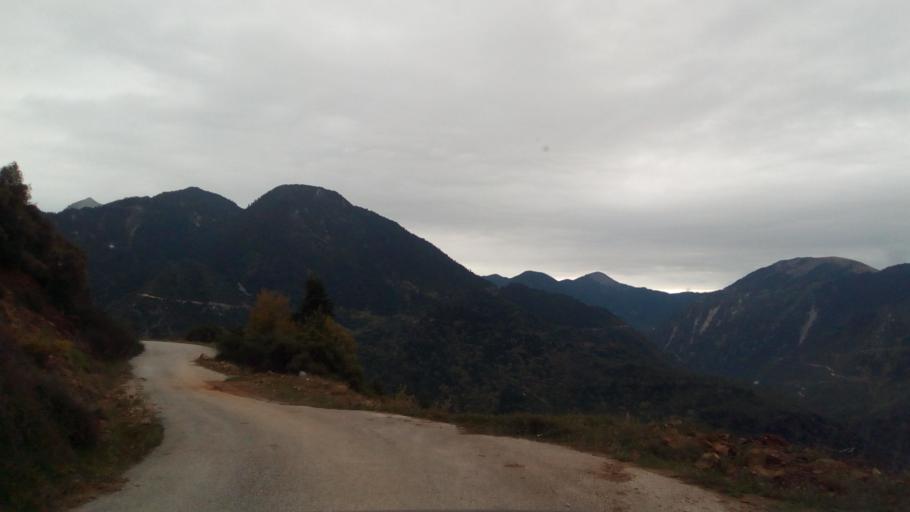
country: GR
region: West Greece
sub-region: Nomos Aitolias kai Akarnanias
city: Thermo
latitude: 38.6060
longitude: 21.8446
